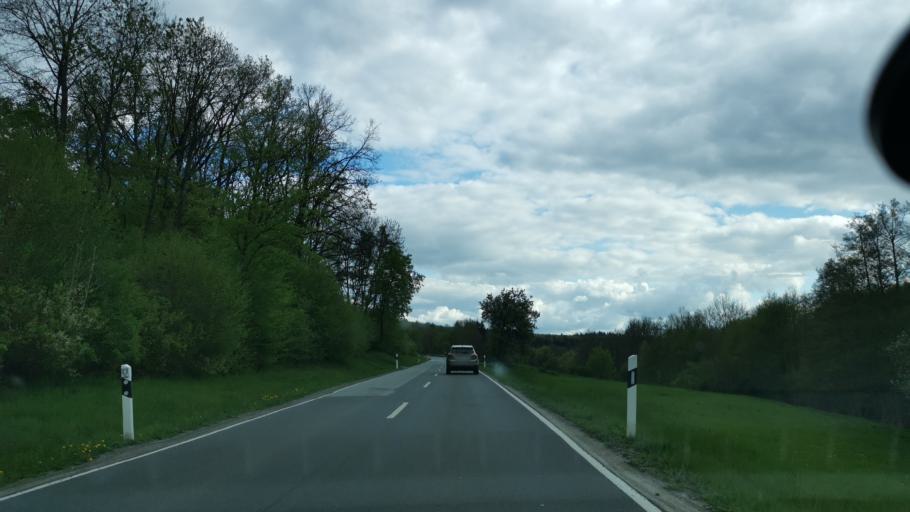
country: DE
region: Baden-Wuerttemberg
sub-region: Karlsruhe Region
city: Osterburken
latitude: 49.4676
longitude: 9.4152
